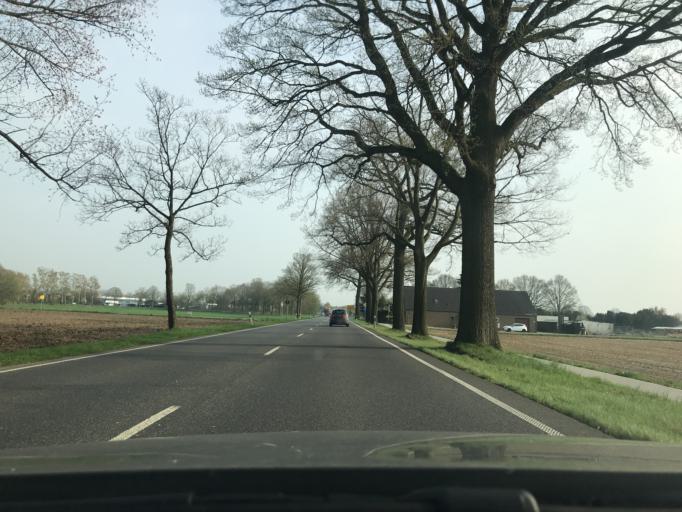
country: DE
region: North Rhine-Westphalia
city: Geldern
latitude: 51.5254
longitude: 6.2861
